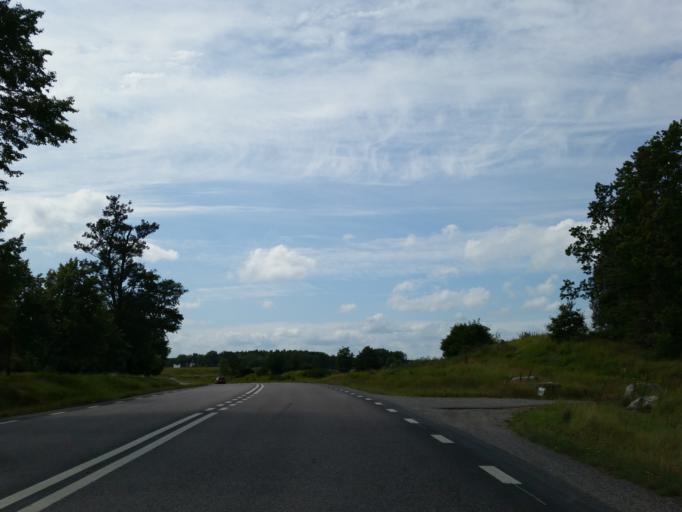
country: SE
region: Soedermanland
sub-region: Strangnas Kommun
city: Mariefred
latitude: 59.2581
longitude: 17.1995
